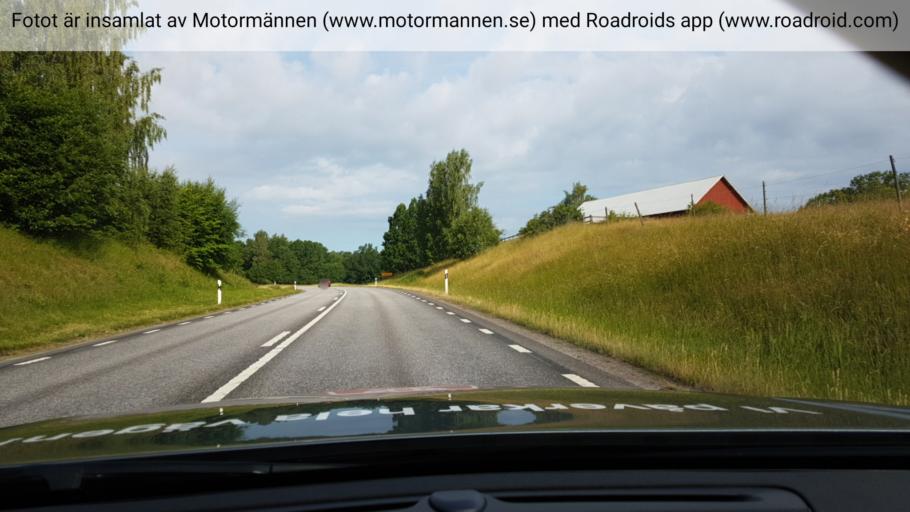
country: SE
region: OEstergoetland
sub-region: Motala Kommun
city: Borensberg
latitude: 58.5358
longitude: 15.3839
